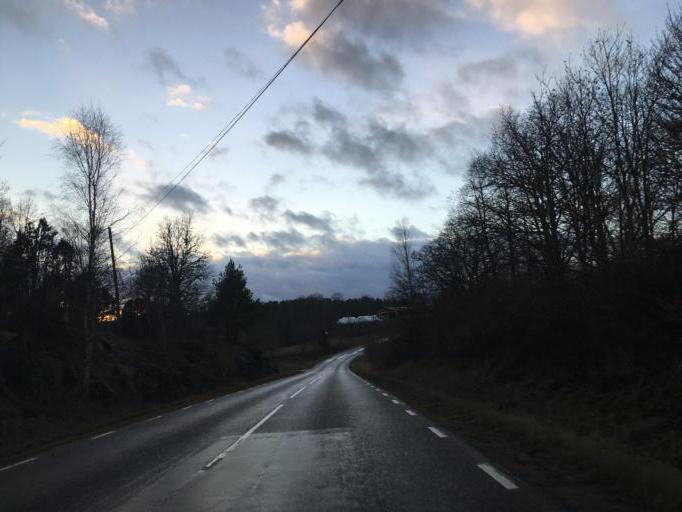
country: SE
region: Kalmar
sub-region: Vasterviks Kommun
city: Vaestervik
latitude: 57.5920
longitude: 16.5123
